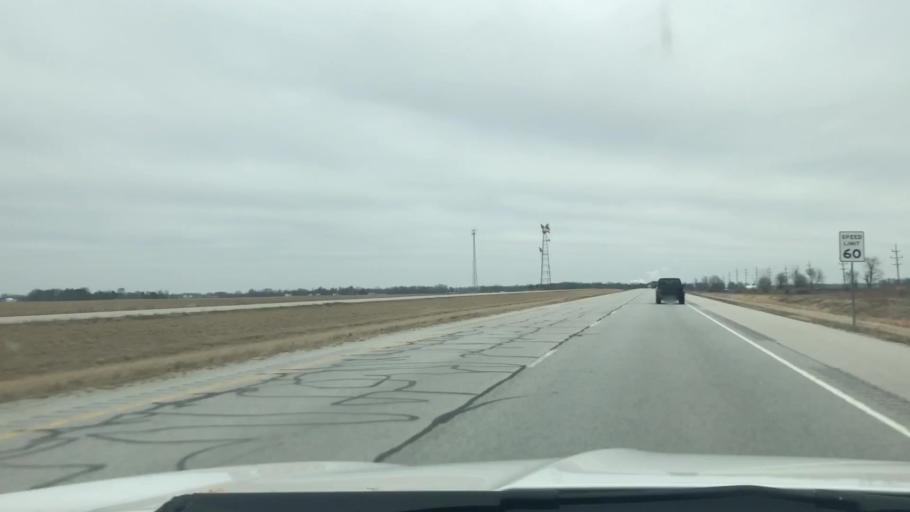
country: US
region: Indiana
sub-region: Cass County
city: Georgetown
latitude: 40.6639
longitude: -86.5325
